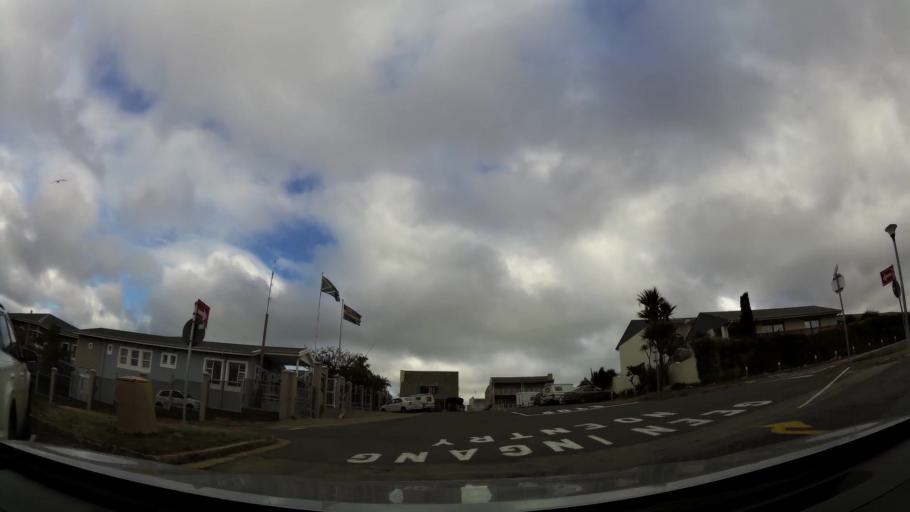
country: ZA
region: Western Cape
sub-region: Eden District Municipality
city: Plettenberg Bay
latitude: -34.0573
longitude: 23.3718
